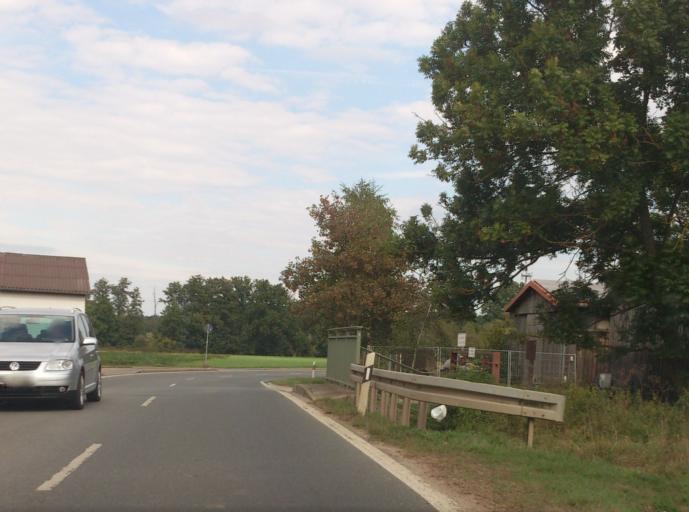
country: DE
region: Bavaria
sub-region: Regierungsbezirk Mittelfranken
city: Wetzendorf
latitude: 49.5215
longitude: 11.0555
